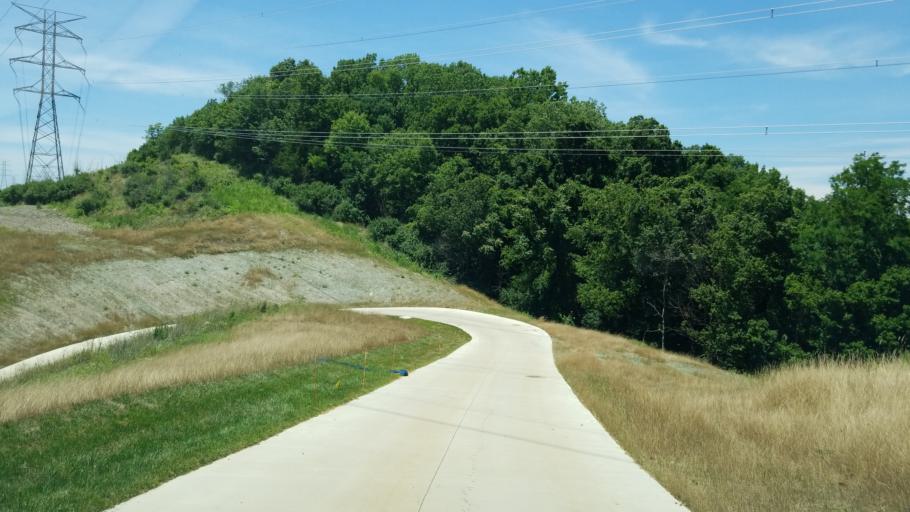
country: US
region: Tennessee
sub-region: Williamson County
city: Brentwood
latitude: 36.0534
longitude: -86.8113
